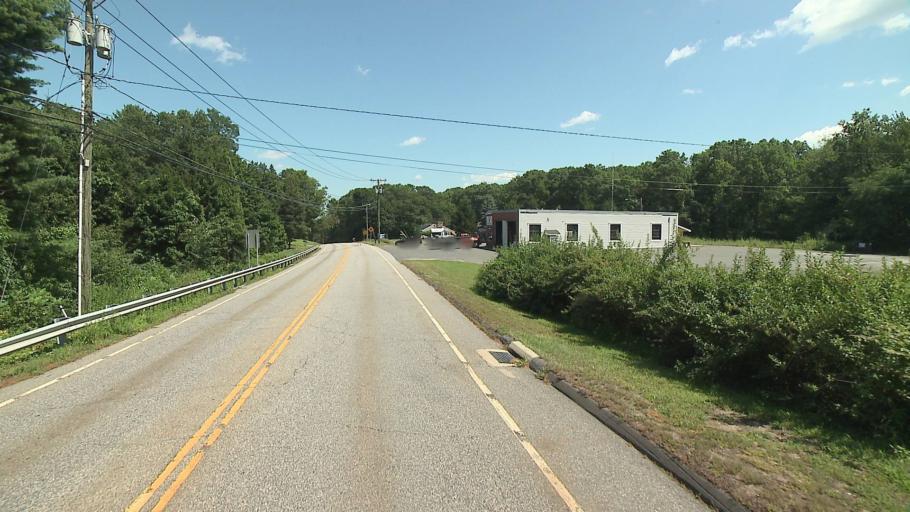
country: US
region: Connecticut
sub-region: Hartford County
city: Collinsville
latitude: 41.7701
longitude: -72.9601
